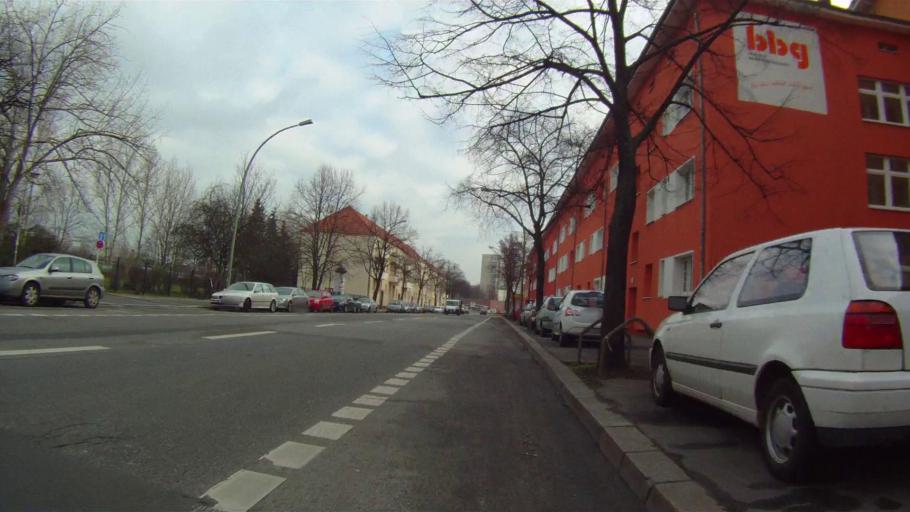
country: DE
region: Berlin
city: Lichtenberg
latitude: 52.5122
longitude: 13.5039
